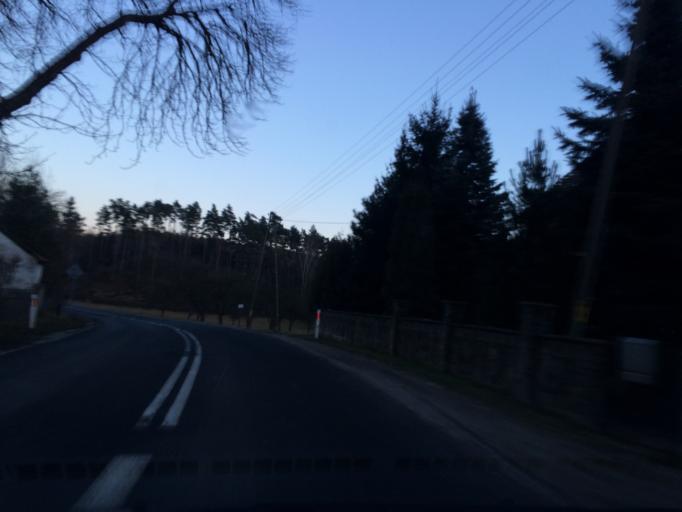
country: PL
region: Lower Silesian Voivodeship
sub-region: Powiat zlotoryjski
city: Olszanica
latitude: 51.1217
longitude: 15.7356
